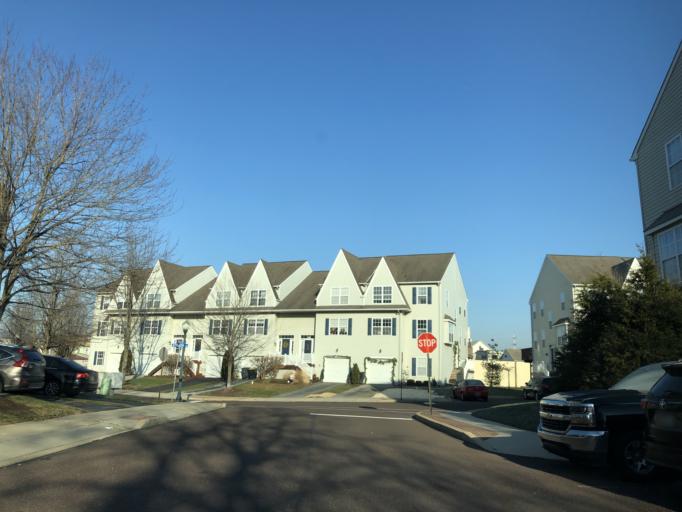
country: US
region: Pennsylvania
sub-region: Chester County
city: Downingtown
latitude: 40.0050
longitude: -75.7000
